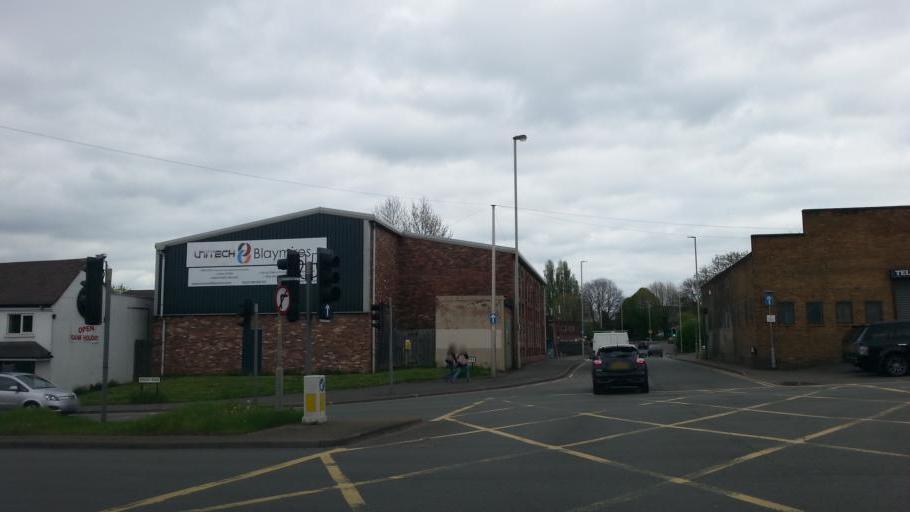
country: GB
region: England
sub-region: Dudley
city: Brierley Hill
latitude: 52.4592
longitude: -2.1177
